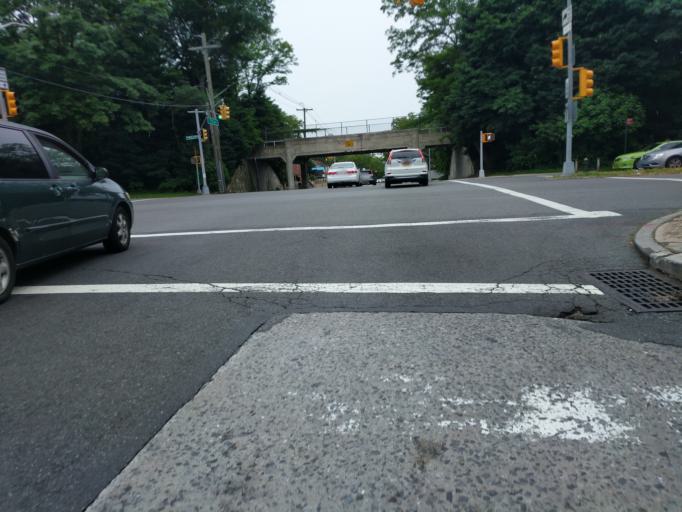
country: US
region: New York
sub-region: Nassau County
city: Bellerose Terrace
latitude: 40.7364
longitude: -73.7726
